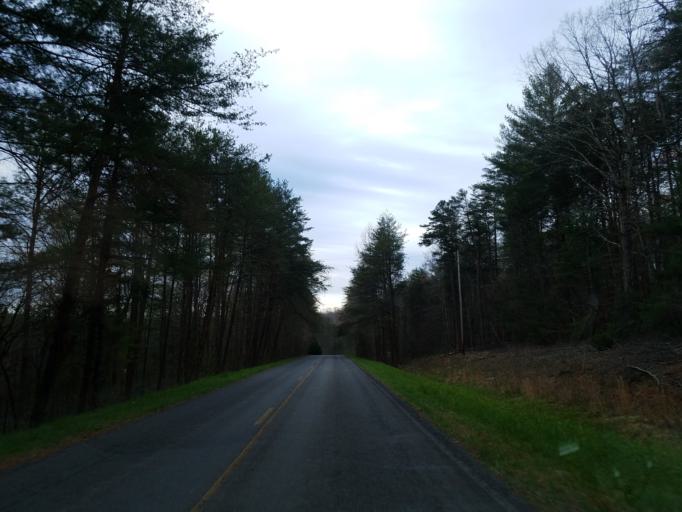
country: US
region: Georgia
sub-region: Fannin County
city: Blue Ridge
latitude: 34.6927
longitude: -84.2993
